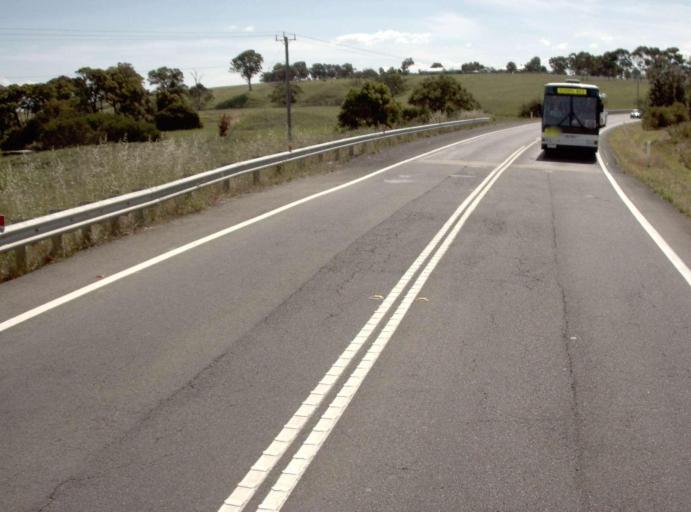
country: AU
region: Victoria
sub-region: East Gippsland
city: Bairnsdale
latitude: -37.8229
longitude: 147.7975
